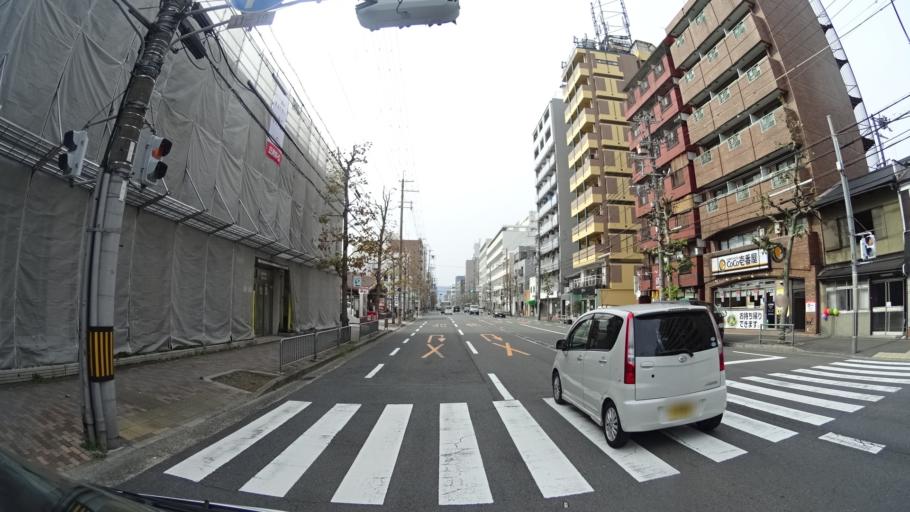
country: JP
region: Kyoto
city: Kyoto
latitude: 35.0037
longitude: 135.7375
